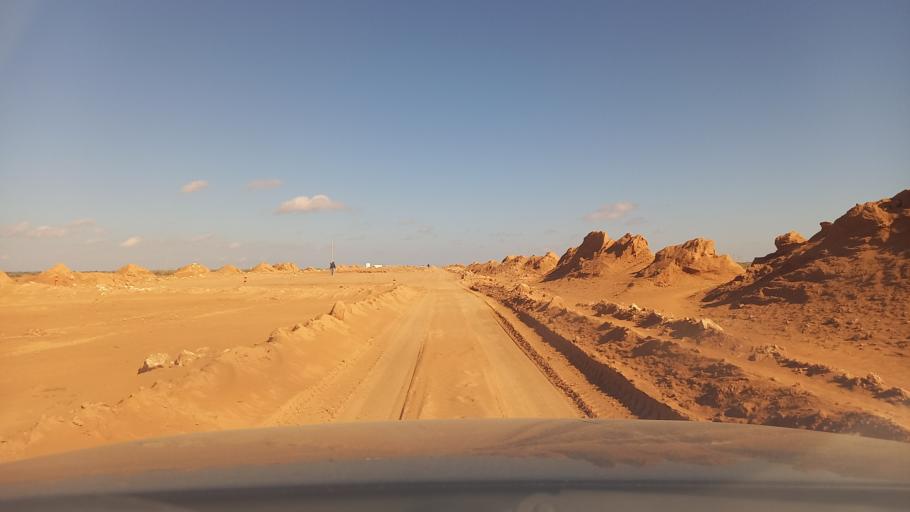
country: TN
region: Madanin
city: Medenine
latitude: 33.2455
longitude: 10.5604
